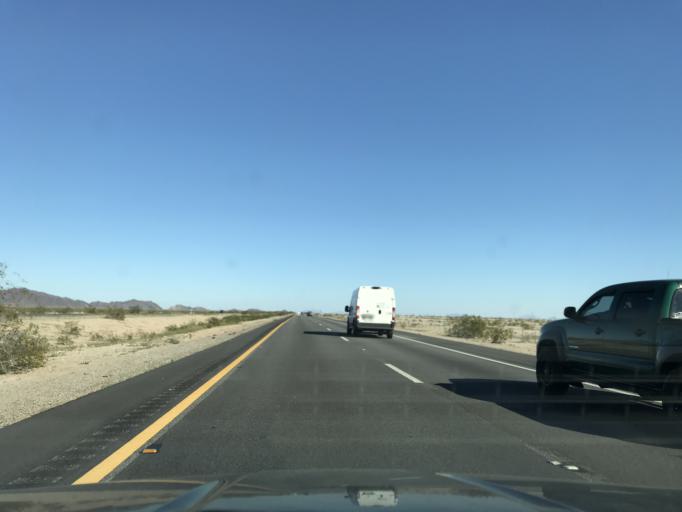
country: US
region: California
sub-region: Riverside County
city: Mesa Verde
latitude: 33.6087
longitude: -114.8713
